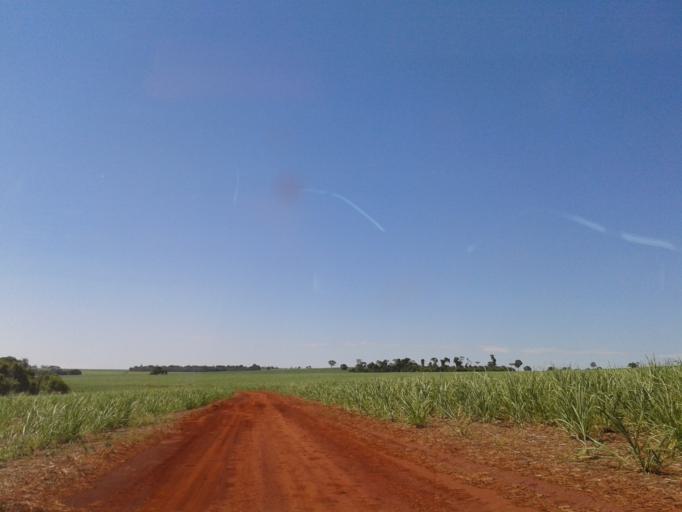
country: BR
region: Minas Gerais
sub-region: Centralina
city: Centralina
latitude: -18.6308
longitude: -49.2596
